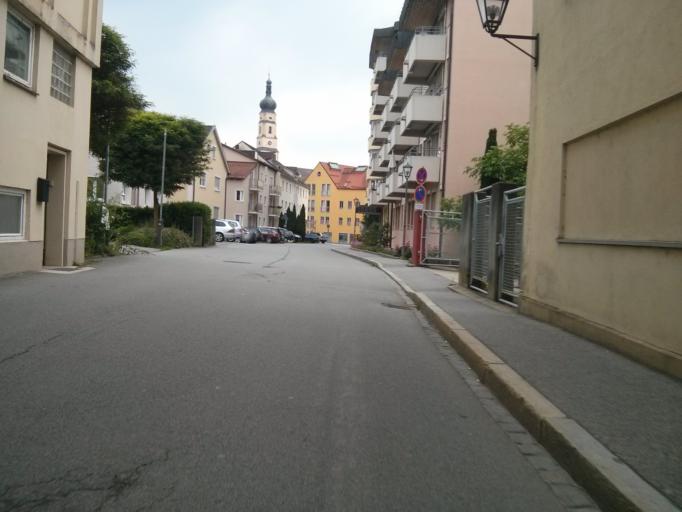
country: DE
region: Bavaria
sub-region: Lower Bavaria
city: Deggendorf
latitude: 48.8314
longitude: 12.9646
